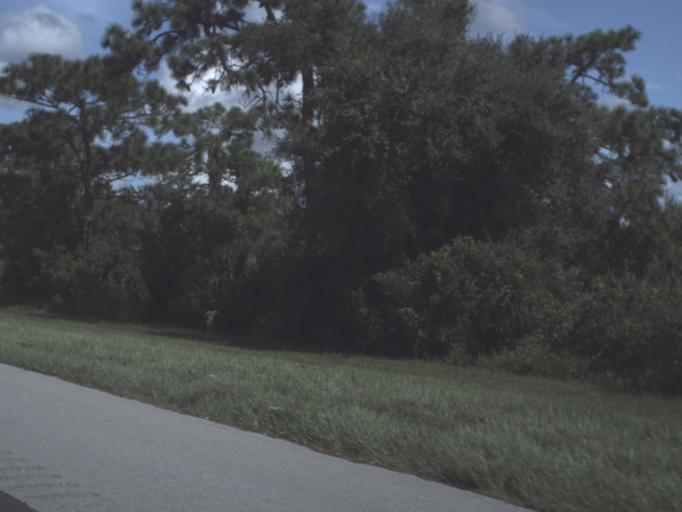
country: US
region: Florida
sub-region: Sarasota County
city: Nokomis
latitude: 27.1467
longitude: -82.4145
